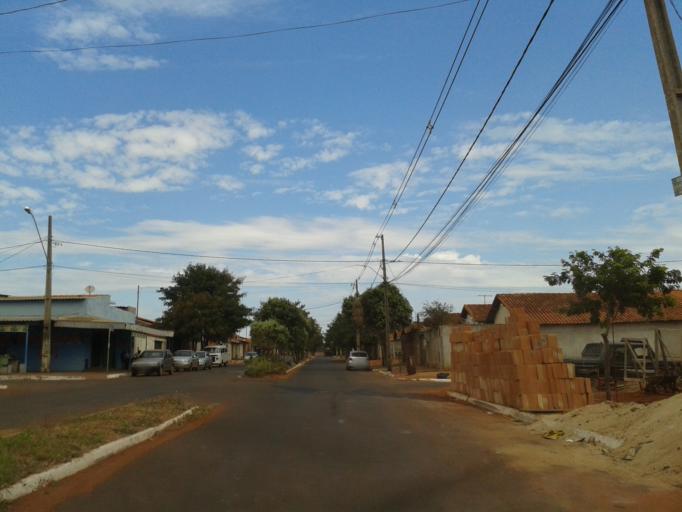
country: BR
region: Minas Gerais
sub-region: Santa Vitoria
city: Santa Vitoria
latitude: -18.8523
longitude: -50.1349
